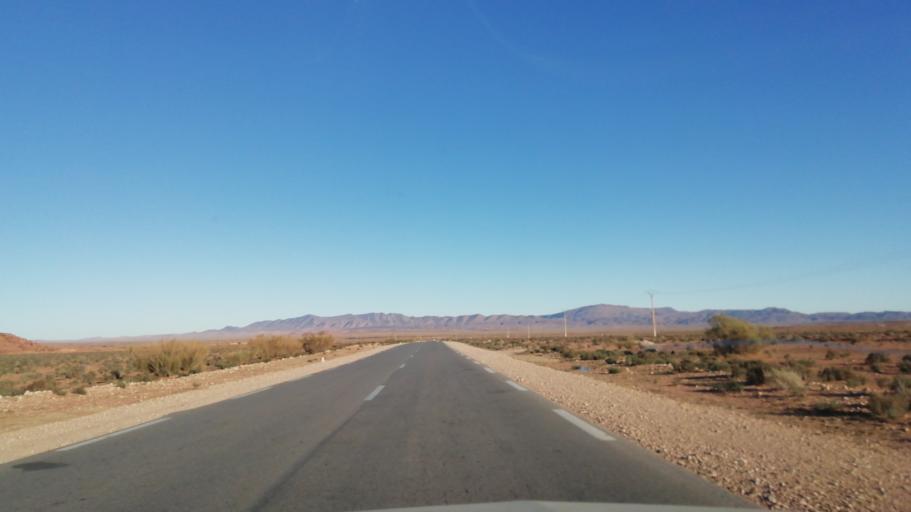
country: DZ
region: El Bayadh
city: El Abiodh Sidi Cheikh
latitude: 33.1698
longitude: 0.5045
